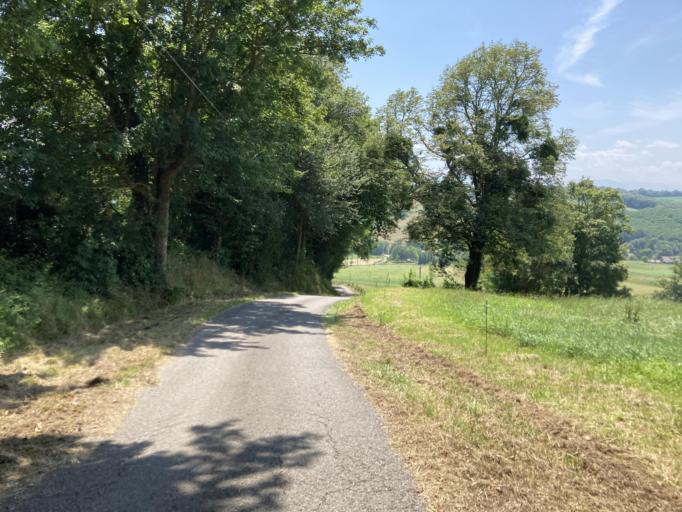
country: FR
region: Aquitaine
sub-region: Departement des Pyrenees-Atlantiques
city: Ledeuix
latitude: 43.2311
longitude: -0.5649
